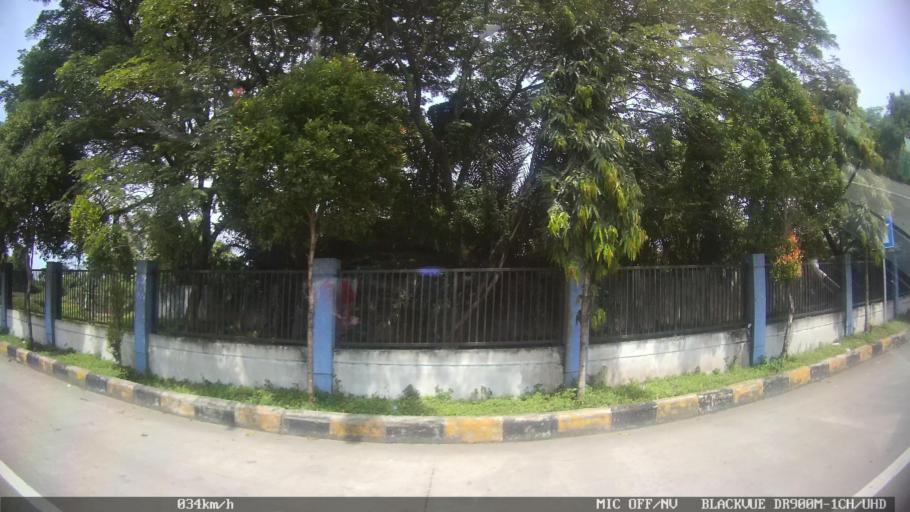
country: ID
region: North Sumatra
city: Medan
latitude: 3.6389
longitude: 98.7090
